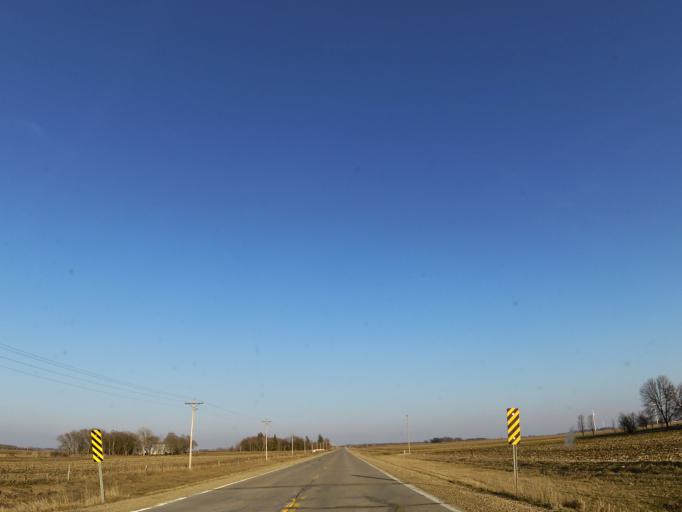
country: US
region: Iowa
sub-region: Worth County
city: Northwood
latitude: 43.4362
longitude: -93.0920
